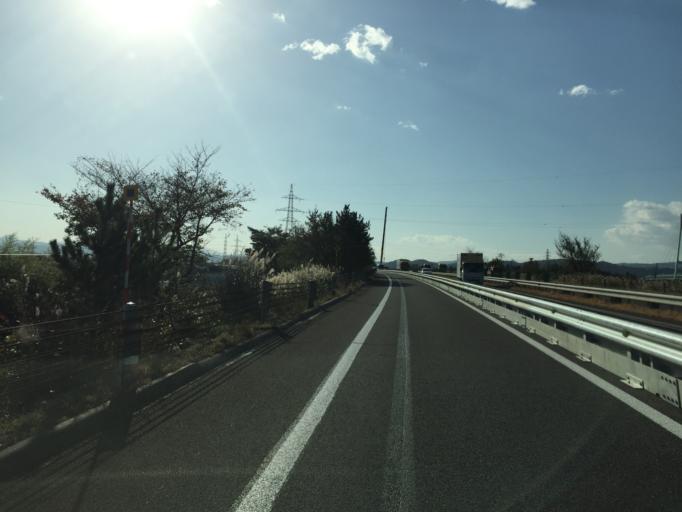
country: JP
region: Fukushima
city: Fukushima-shi
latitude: 37.7522
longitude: 140.4095
